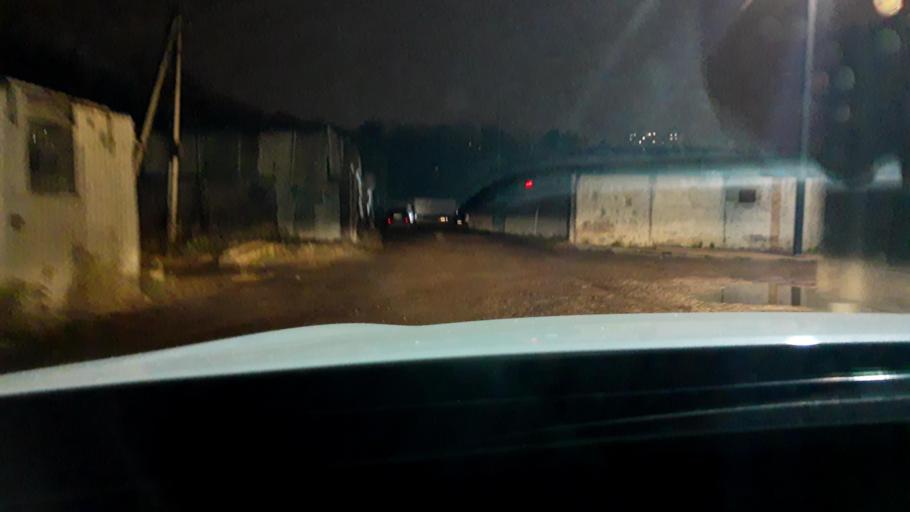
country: RU
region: Moskovskaya
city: Krasnogorsk
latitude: 55.8402
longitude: 37.3407
